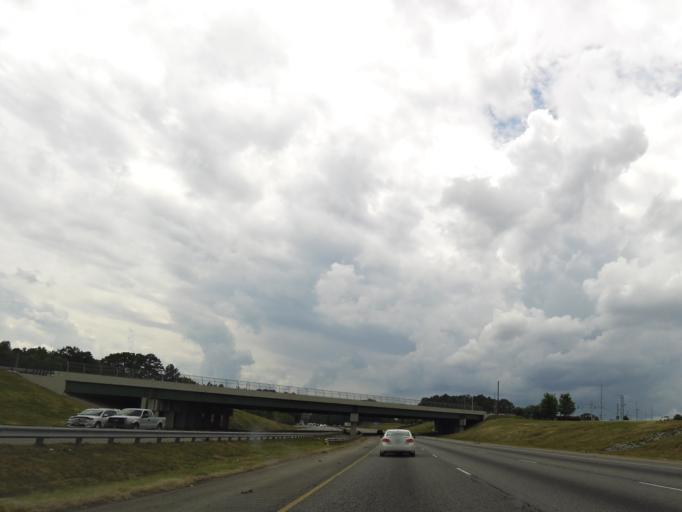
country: US
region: Georgia
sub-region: Douglas County
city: Douglasville
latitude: 33.7515
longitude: -84.7142
